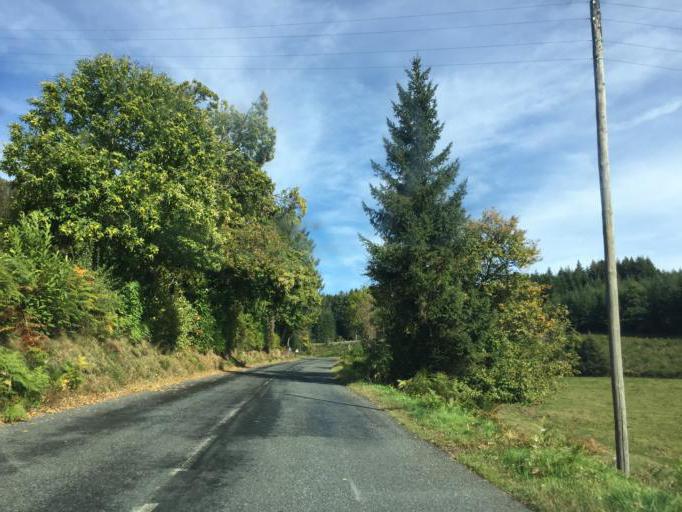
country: FR
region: Rhone-Alpes
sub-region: Departement de la Loire
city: Belmont-de-la-Loire
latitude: 46.1328
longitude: 4.4050
